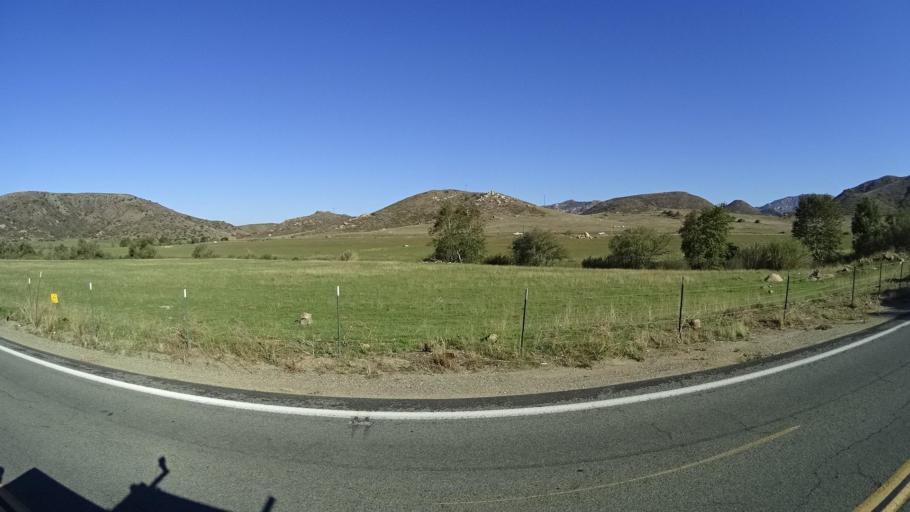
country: US
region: California
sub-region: San Diego County
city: Jamul
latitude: 32.6679
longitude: -116.8287
